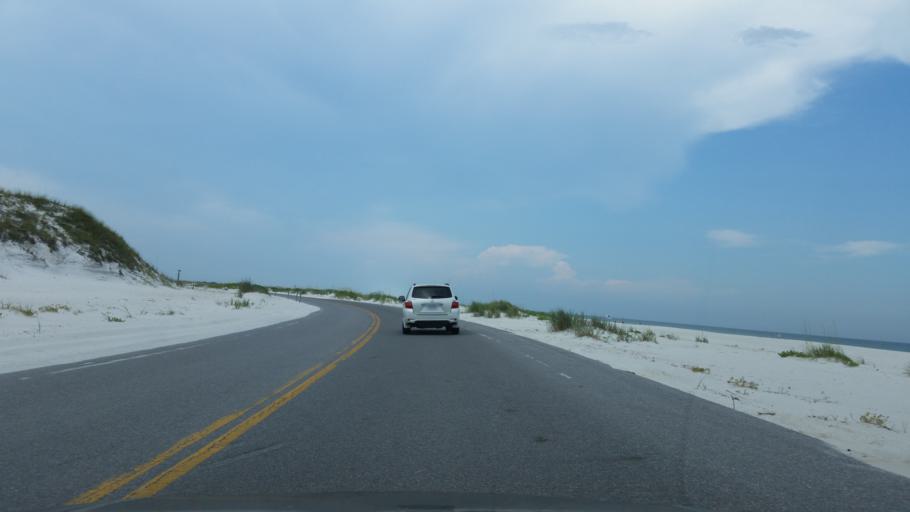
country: US
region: Florida
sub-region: Santa Rosa County
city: Woodlawn Beach
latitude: 30.3673
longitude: -86.9427
